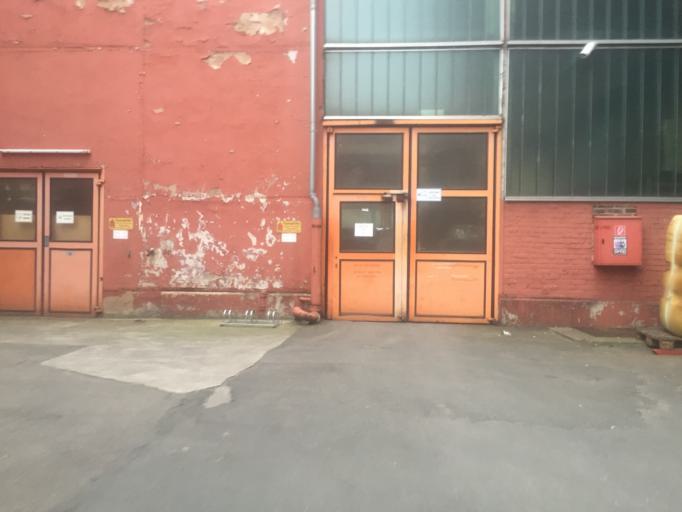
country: DE
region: Baden-Wuerttemberg
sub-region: Karlsruhe Region
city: Mannheim
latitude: 49.5081
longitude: 8.4991
